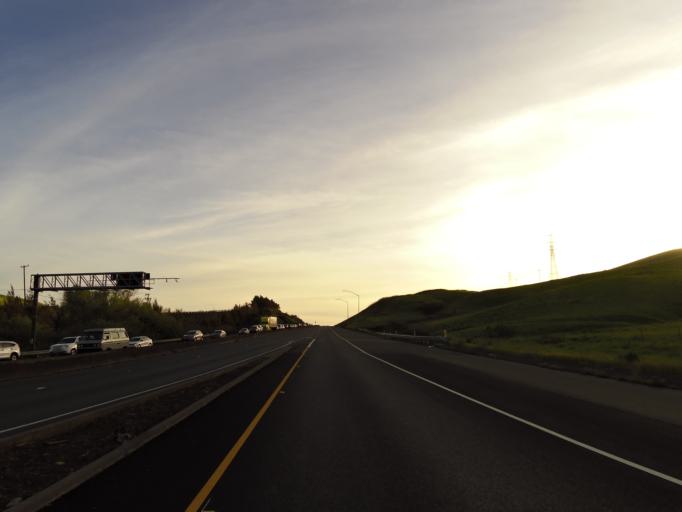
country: US
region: California
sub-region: Marin County
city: Black Point-Green Point
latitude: 38.1506
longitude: -122.4505
